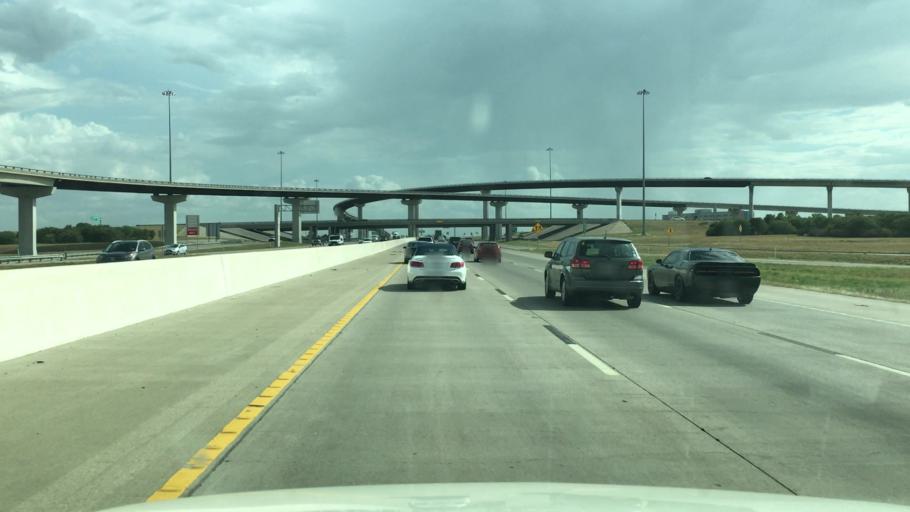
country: US
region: Texas
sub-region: McLennan County
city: Beverly Hills
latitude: 31.4964
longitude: -97.1492
